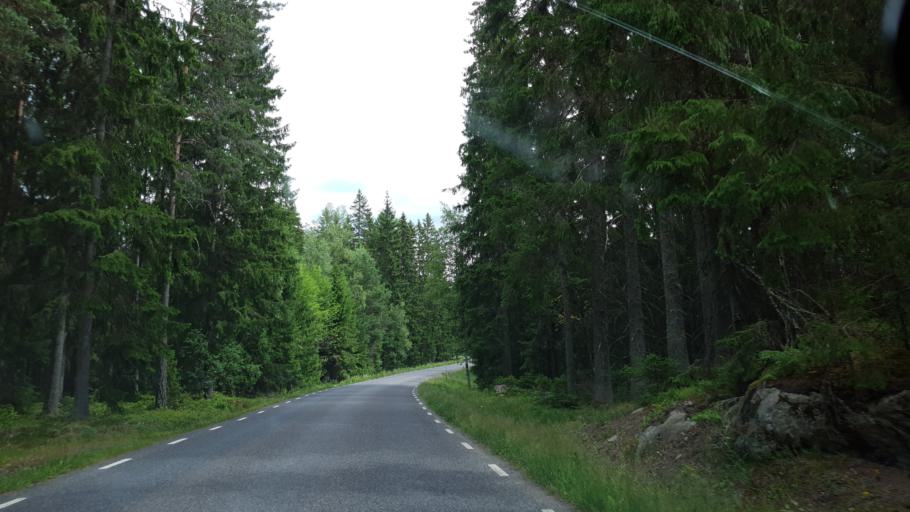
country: SE
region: Kronoberg
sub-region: Uppvidinge Kommun
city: Aseda
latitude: 57.1915
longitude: 15.3964
